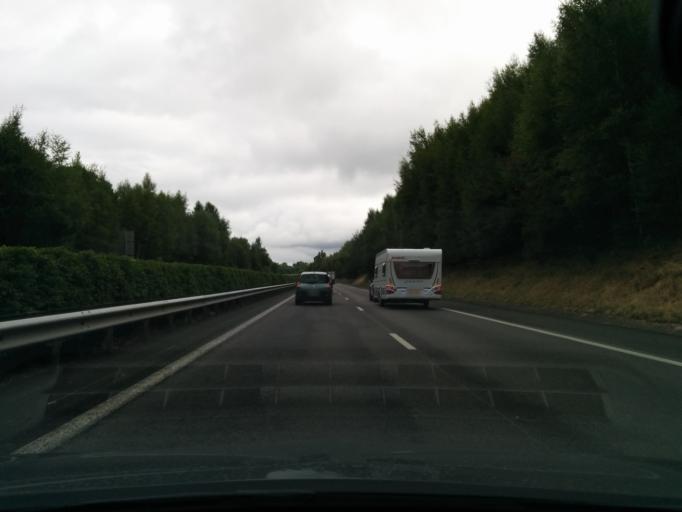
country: FR
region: Limousin
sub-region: Departement de la Correze
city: Donzenac
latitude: 45.2646
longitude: 1.5487
